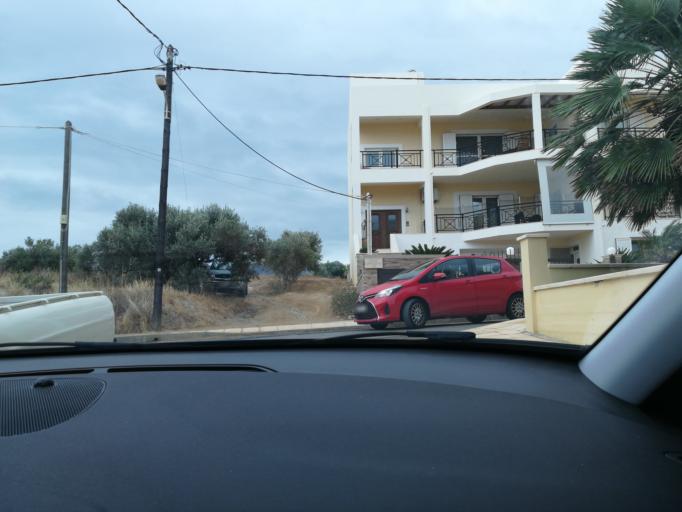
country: GR
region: Crete
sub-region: Nomos Lasithiou
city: Siteia
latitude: 35.2031
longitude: 26.0990
